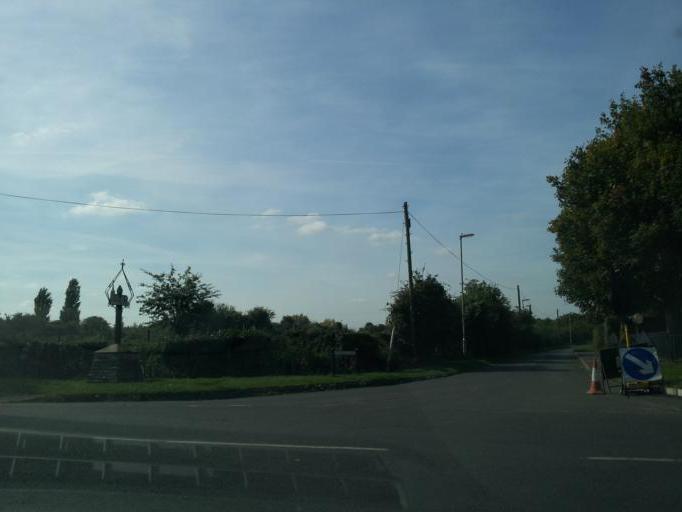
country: GB
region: England
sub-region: Cambridgeshire
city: Waterbeach
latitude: 52.2645
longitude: 0.1624
